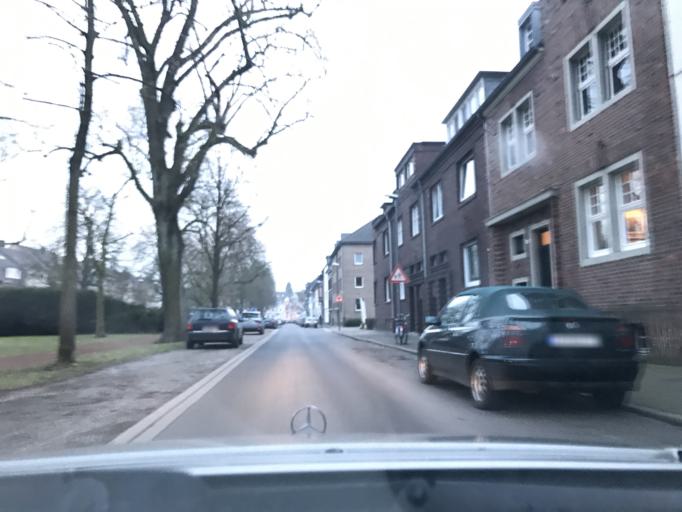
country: DE
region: North Rhine-Westphalia
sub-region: Regierungsbezirk Dusseldorf
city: Krefeld
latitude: 51.3429
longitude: 6.5759
